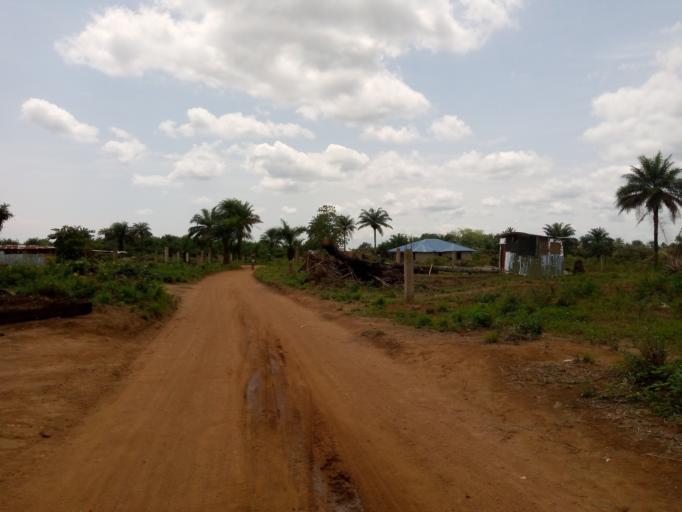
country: SL
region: Western Area
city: Waterloo
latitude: 8.3421
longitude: -13.0114
